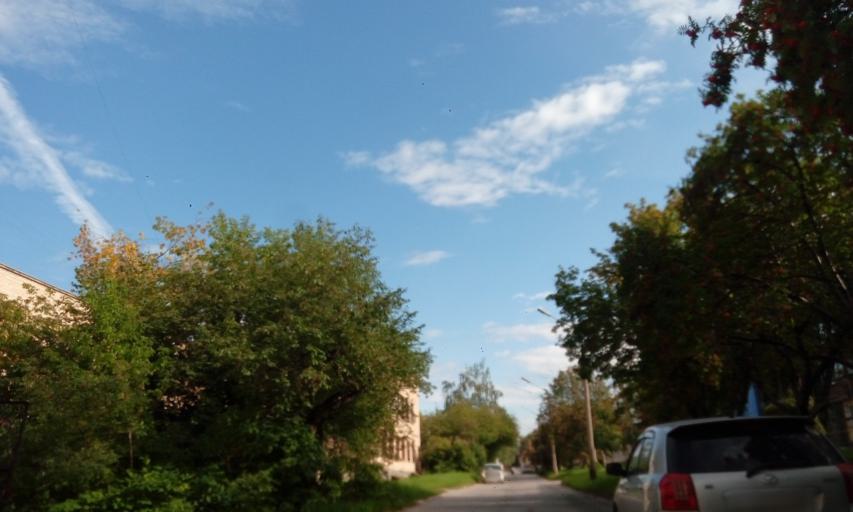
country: RU
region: Novosibirsk
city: Akademgorodok
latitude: 54.8410
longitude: 83.0924
